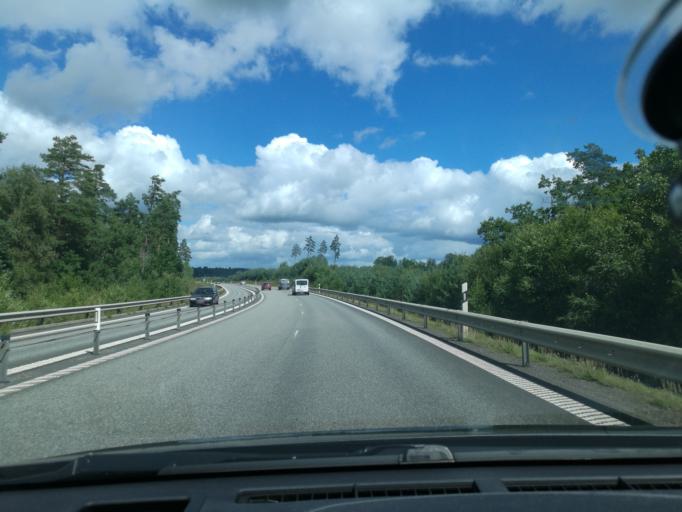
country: SE
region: Skane
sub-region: Hassleholms Kommun
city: Hassleholm
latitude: 56.1723
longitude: 13.8395
